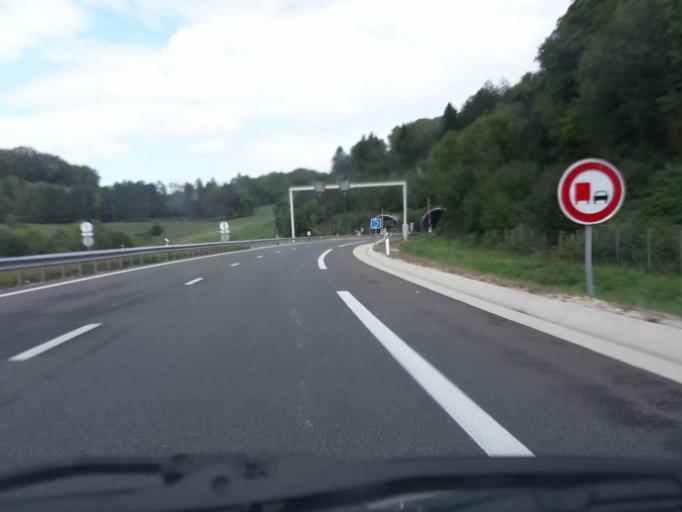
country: FR
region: Franche-Comte
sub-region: Departement du Doubs
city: Morre
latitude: 47.2111
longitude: 6.0509
